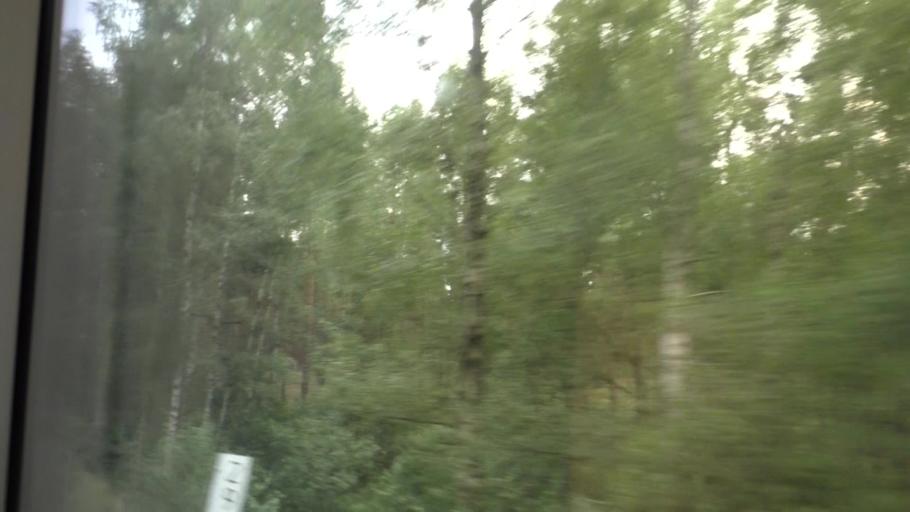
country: DE
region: Brandenburg
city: Wendisch Rietz
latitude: 52.2163
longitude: 13.9927
